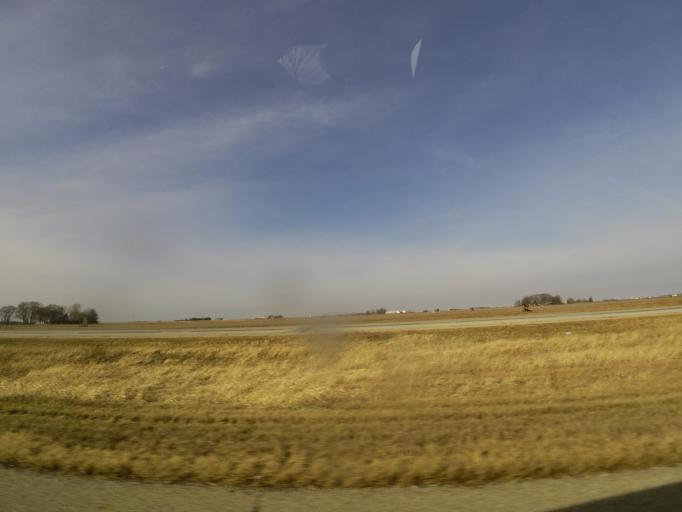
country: US
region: Illinois
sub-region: Macon County
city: Harristown
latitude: 39.8616
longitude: -89.0436
